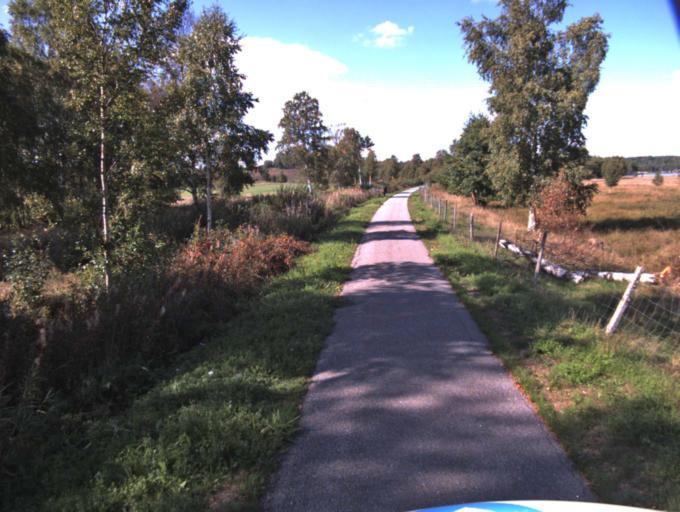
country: SE
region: Vaestra Goetaland
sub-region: Ulricehamns Kommun
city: Ulricehamn
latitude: 57.8388
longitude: 13.3062
